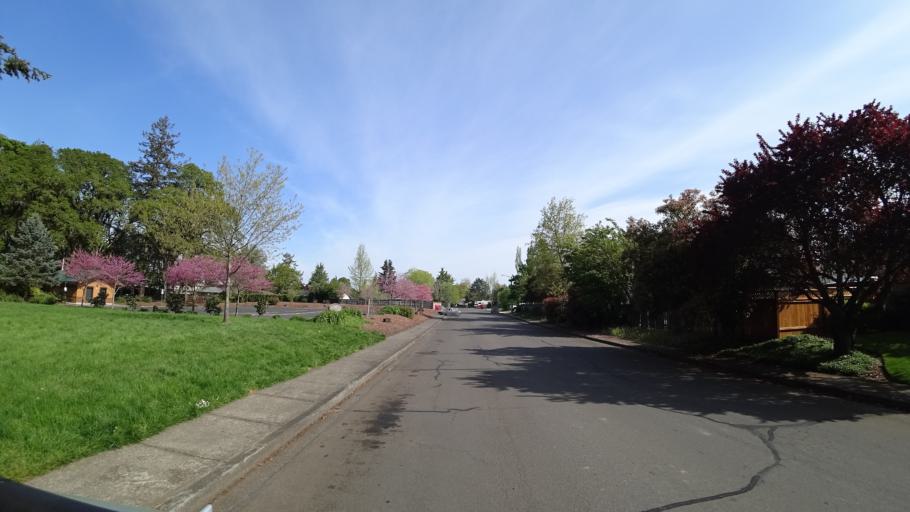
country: US
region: Oregon
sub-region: Washington County
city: Hillsboro
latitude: 45.5269
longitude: -122.9585
